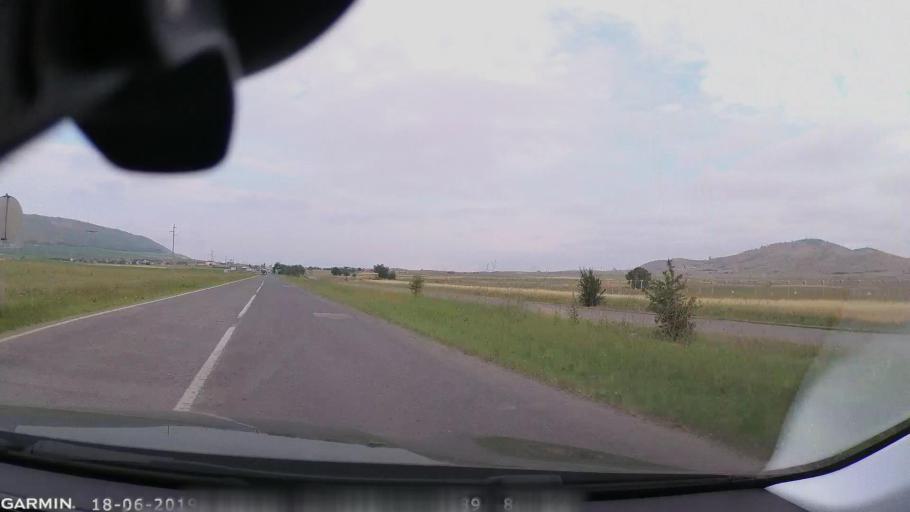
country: MK
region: Stip
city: Shtip
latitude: 41.7679
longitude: 22.1519
